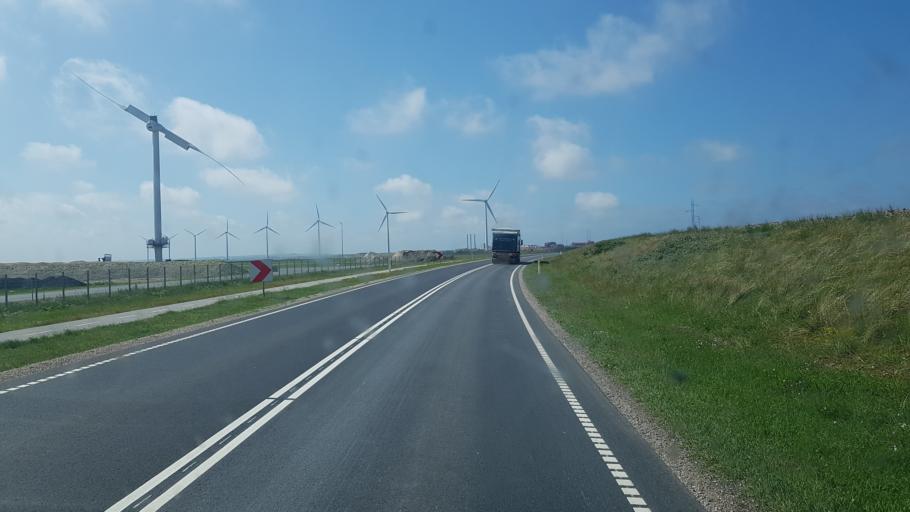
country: DK
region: Central Jutland
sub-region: Lemvig Kommune
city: Thyboron
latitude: 56.6793
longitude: 8.2232
